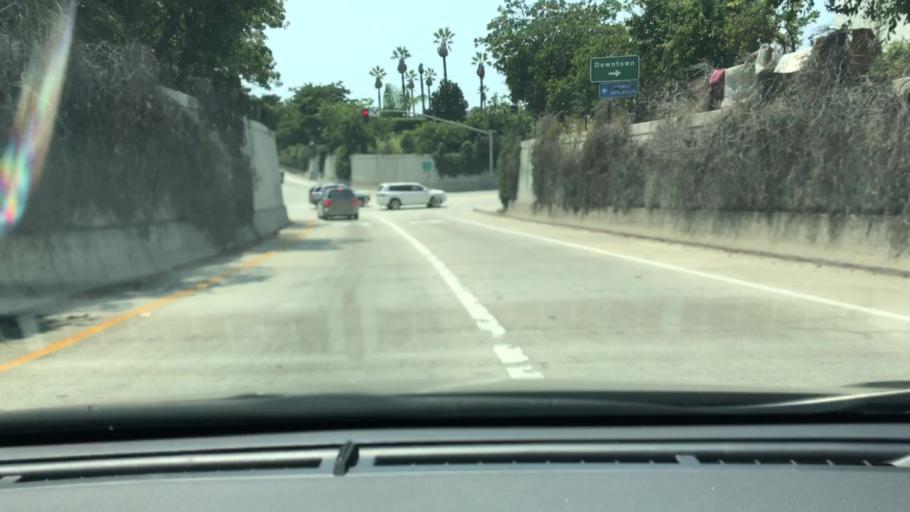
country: US
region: California
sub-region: Santa Barbara County
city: Santa Barbara
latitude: 34.4189
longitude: -119.6896
